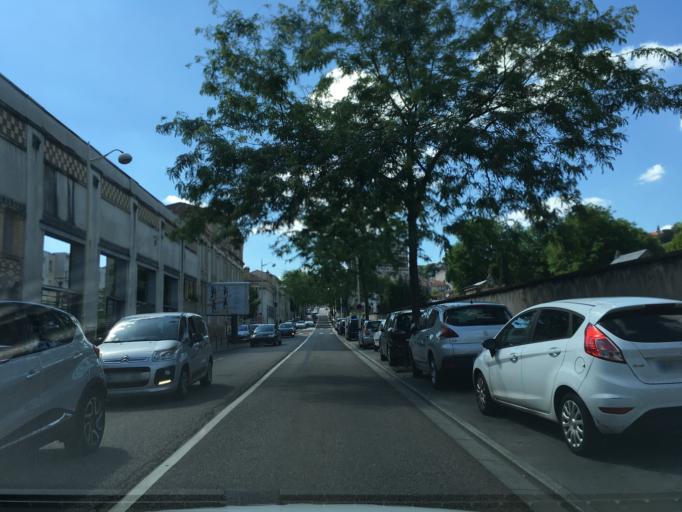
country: FR
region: Lorraine
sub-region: Departement de Meurthe-et-Moselle
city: Laxou
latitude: 48.6885
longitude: 6.1650
